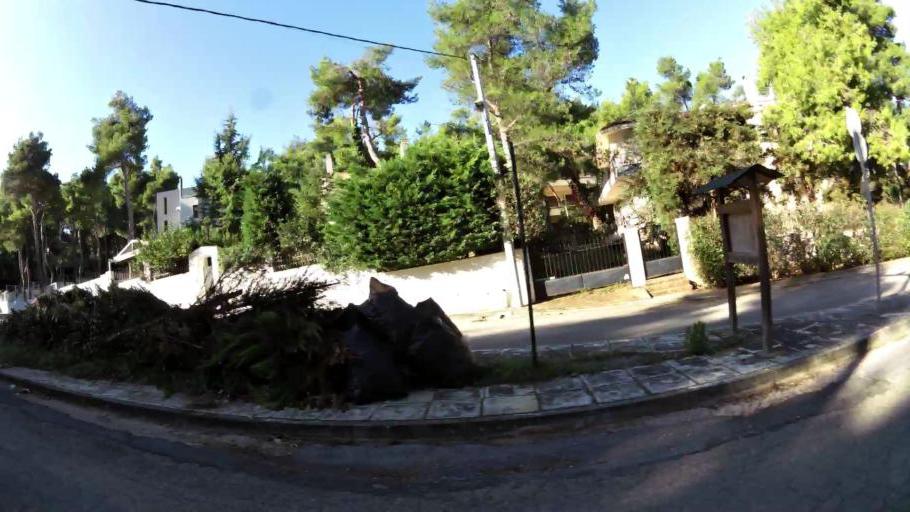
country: GR
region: Attica
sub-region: Nomarchia Anatolikis Attikis
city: Stamata
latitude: 38.1349
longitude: 23.8768
